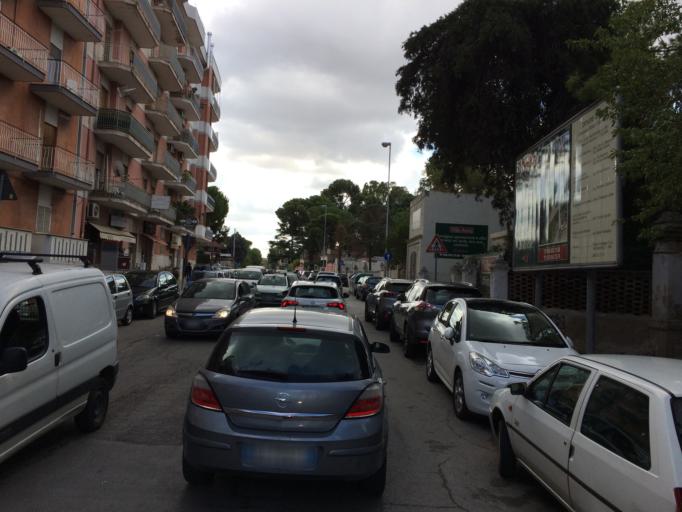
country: IT
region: Apulia
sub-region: Provincia di Bari
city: Bari
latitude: 41.1003
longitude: 16.8800
